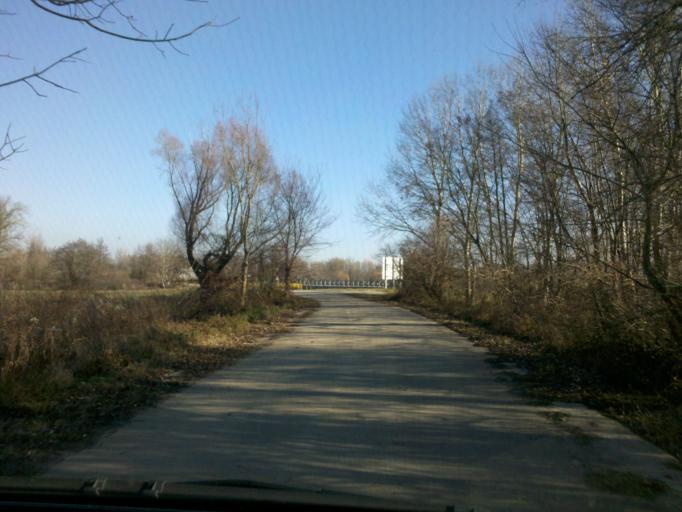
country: HR
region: Medimurska
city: Gorican
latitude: 46.4090
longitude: 16.6847
